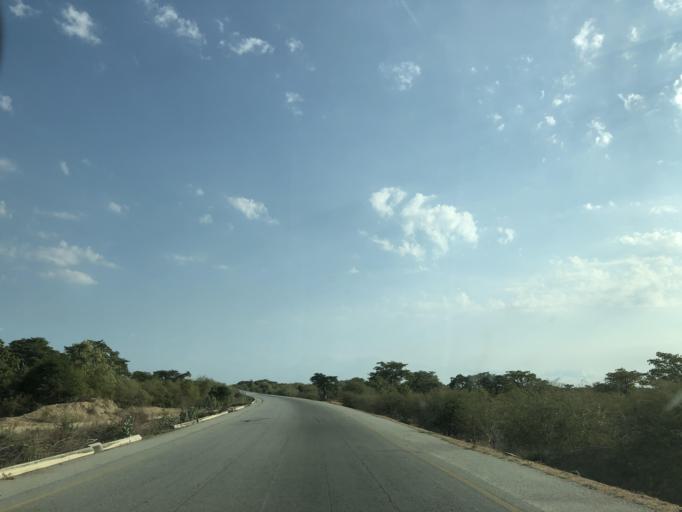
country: AO
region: Benguela
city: Benguela
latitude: -13.1881
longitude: 13.7624
